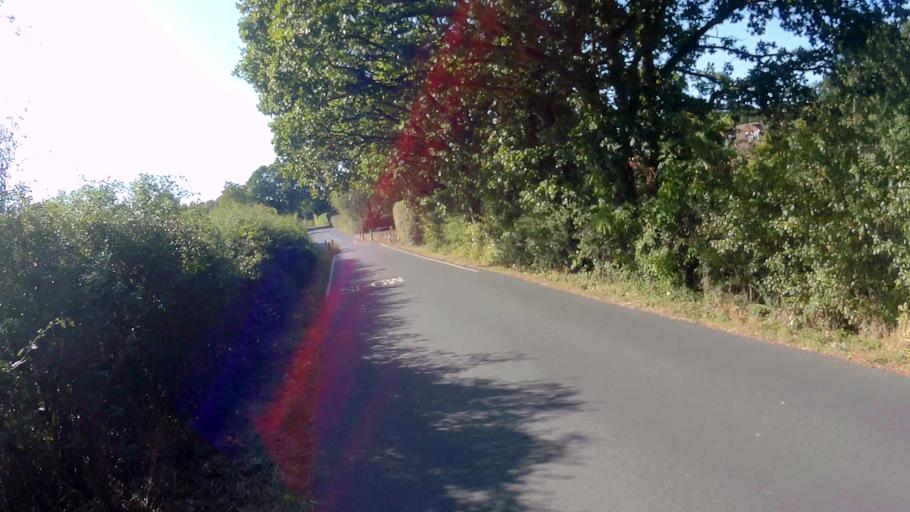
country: GB
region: England
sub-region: Hampshire
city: Lindford
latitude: 51.1587
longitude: -0.8196
